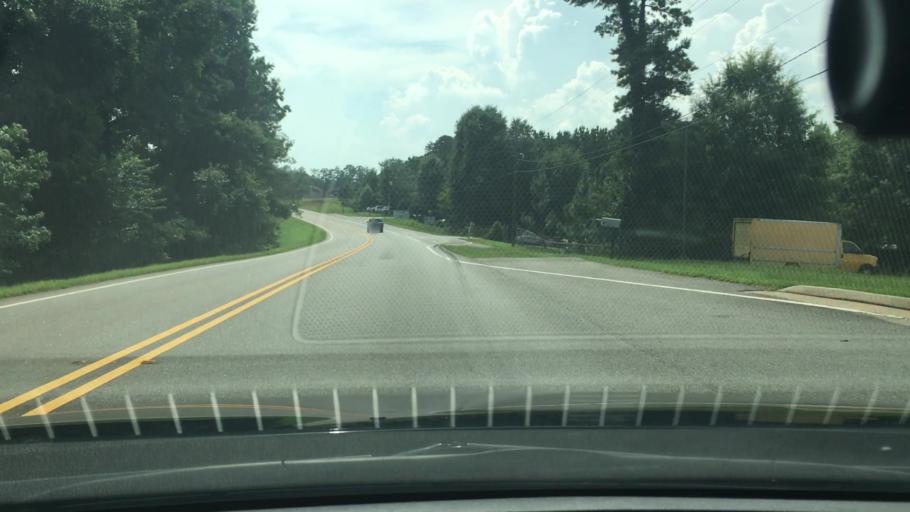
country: US
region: Georgia
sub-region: Coweta County
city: East Newnan
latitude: 33.3362
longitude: -84.7456
